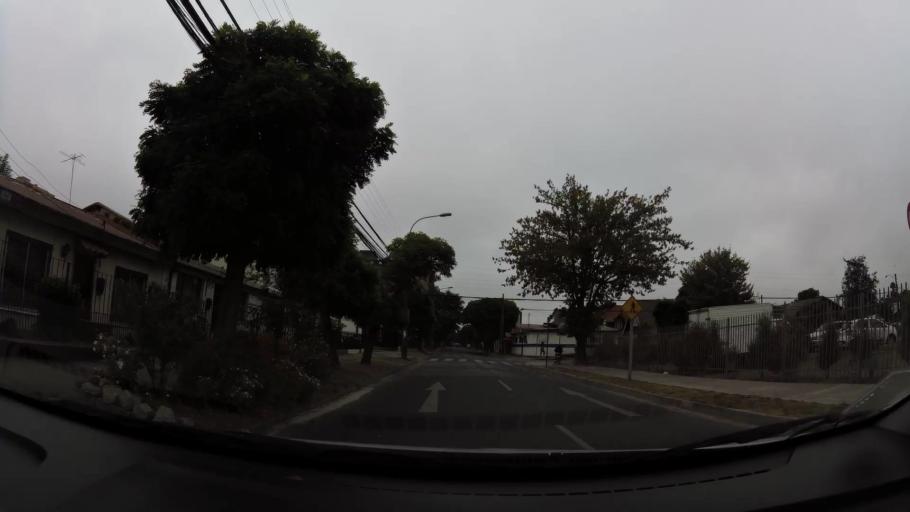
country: CL
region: Biobio
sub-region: Provincia de Concepcion
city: Concepcion
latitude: -36.8145
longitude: -73.0338
